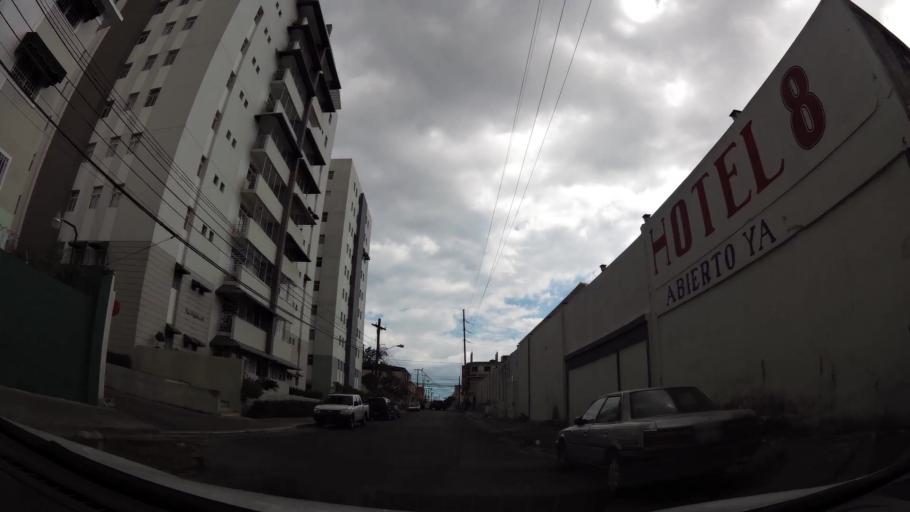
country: DO
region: Nacional
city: San Carlos
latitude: 18.4900
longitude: -69.9170
